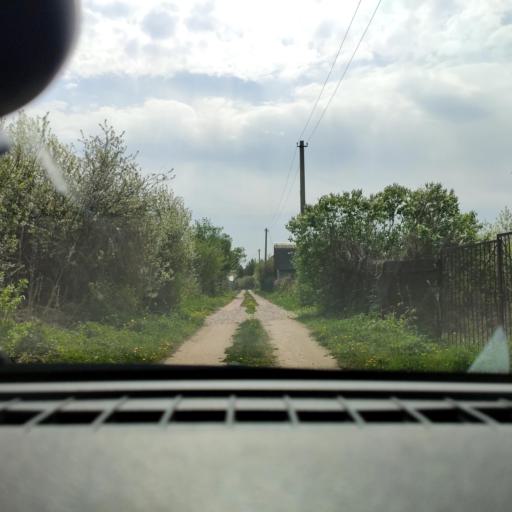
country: RU
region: Samara
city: Tol'yatti
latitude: 53.7064
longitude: 49.4130
